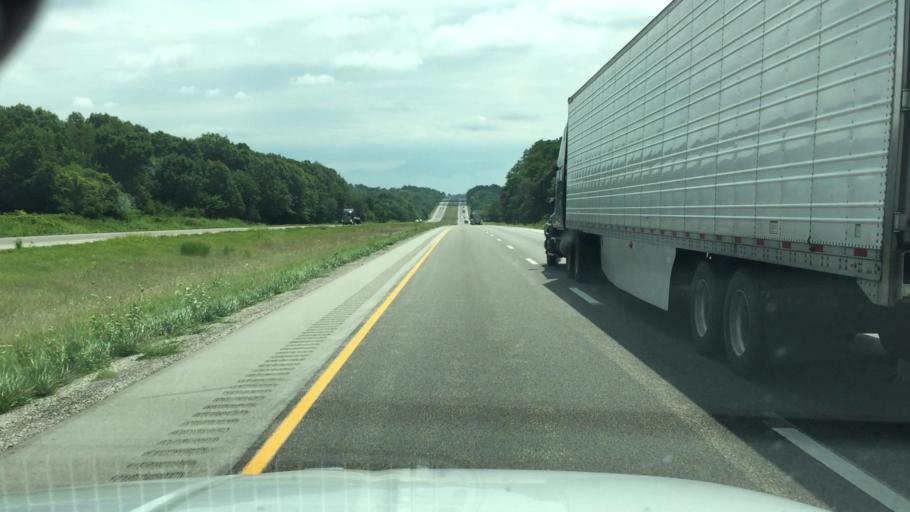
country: US
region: Illinois
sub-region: Peoria County
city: Elmwood
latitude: 40.8635
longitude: -90.0192
